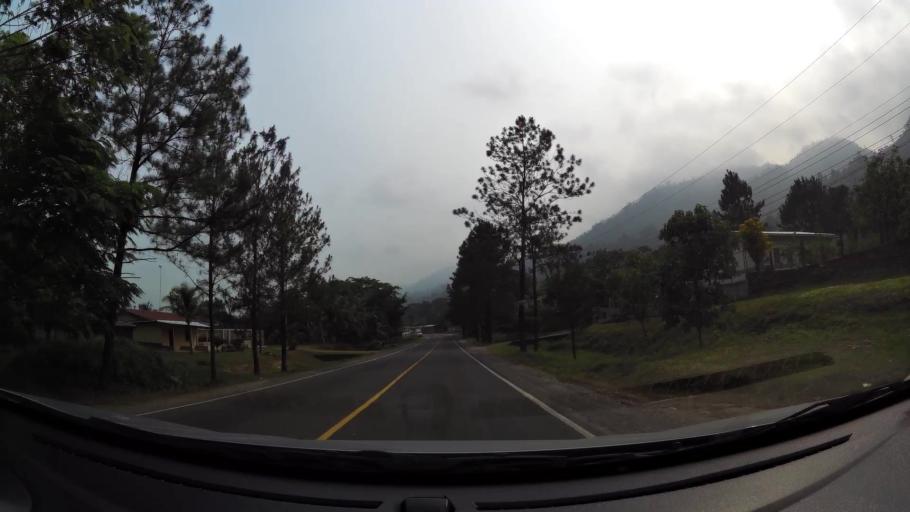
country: HN
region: Atlantida
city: Mezapa
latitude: 15.5922
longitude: -87.6096
